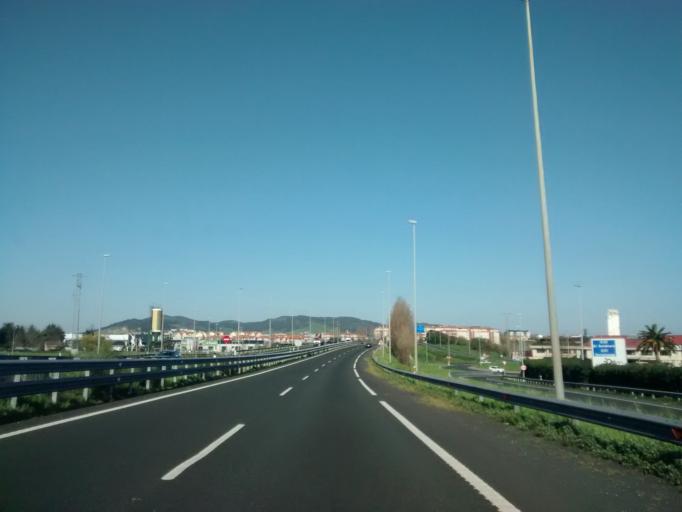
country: ES
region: Cantabria
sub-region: Provincia de Cantabria
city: Santa Cruz de Bezana
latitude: 43.4389
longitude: -3.8862
